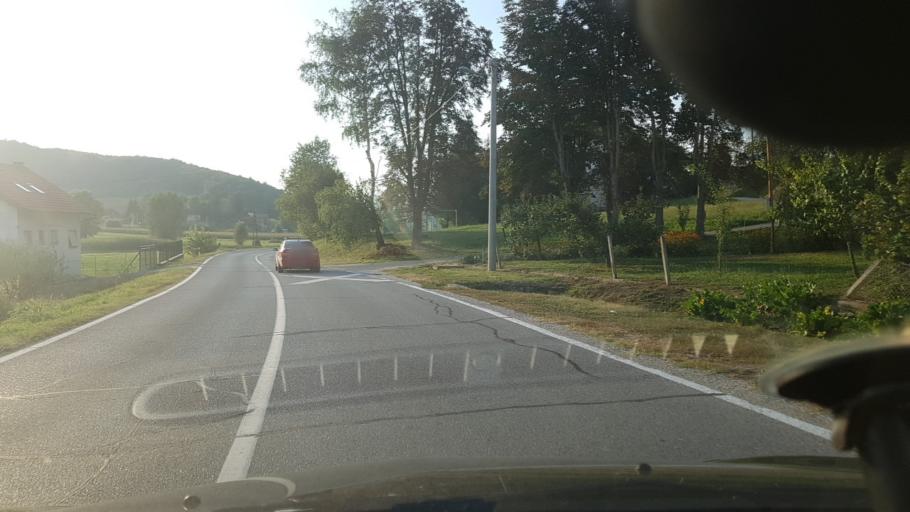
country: HR
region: Krapinsko-Zagorska
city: Pregrada
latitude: 46.1359
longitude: 15.7943
